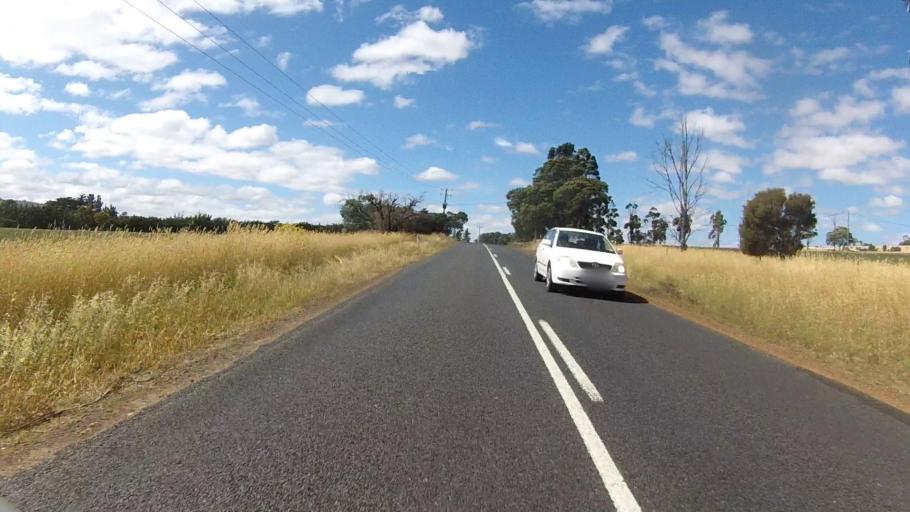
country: AU
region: Tasmania
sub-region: Sorell
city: Sorell
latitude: -42.6096
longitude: 147.4247
